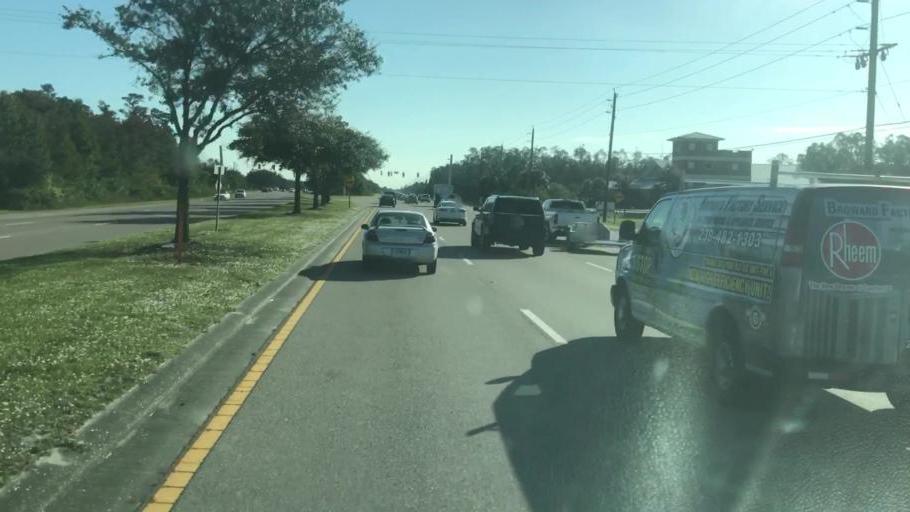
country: US
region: Florida
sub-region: Lee County
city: Villas
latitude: 26.5469
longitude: -81.8189
